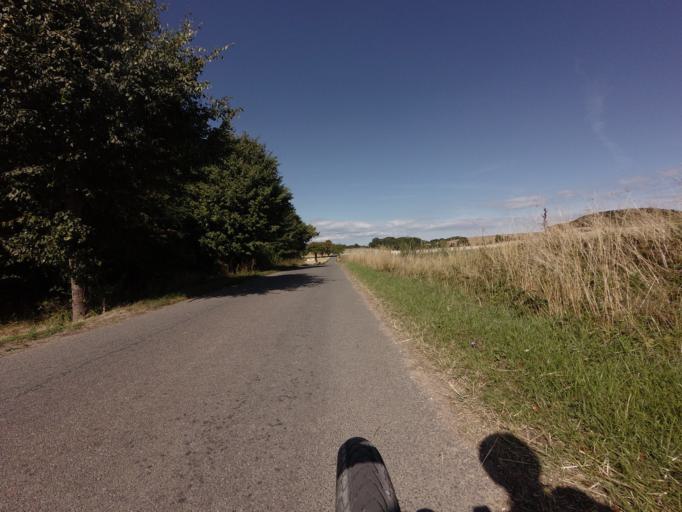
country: DK
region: Zealand
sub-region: Vordingborg Kommune
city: Stege
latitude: 55.0120
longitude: 12.4600
